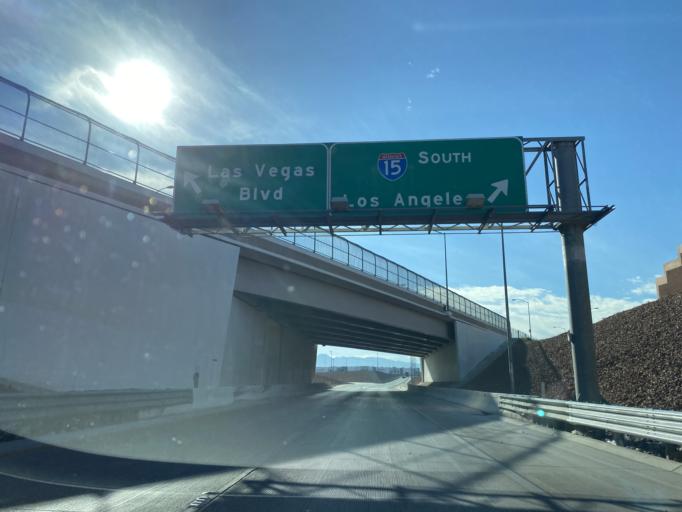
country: US
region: Nevada
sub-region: Clark County
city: Paradise
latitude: 36.0638
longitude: -115.1846
